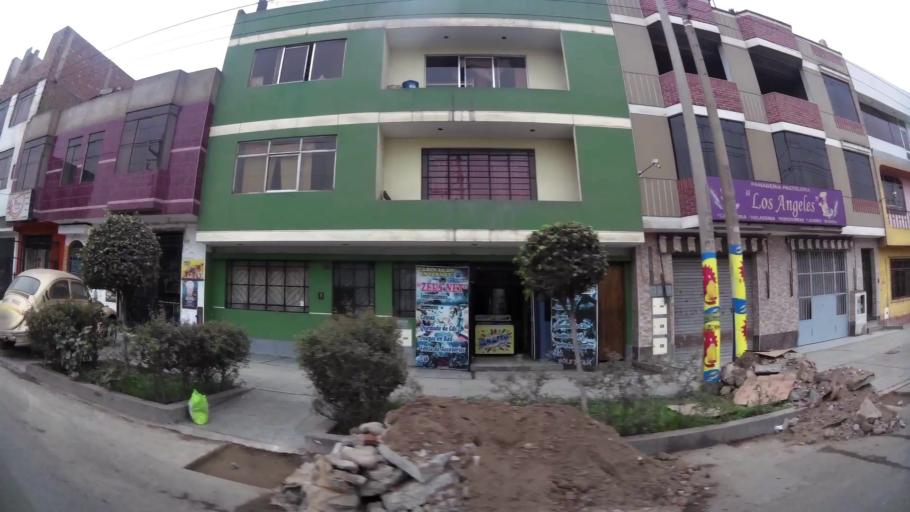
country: PE
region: Lima
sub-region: Lima
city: Vitarte
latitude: -12.0354
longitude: -76.9353
